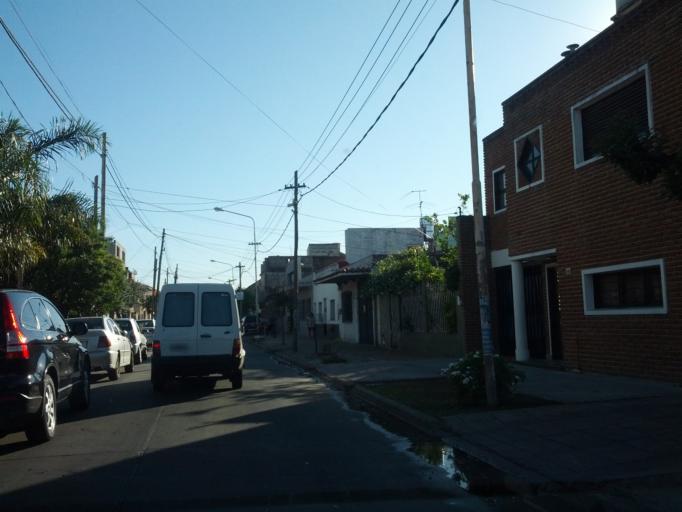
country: AR
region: Buenos Aires
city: San Justo
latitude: -34.6637
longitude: -58.5362
